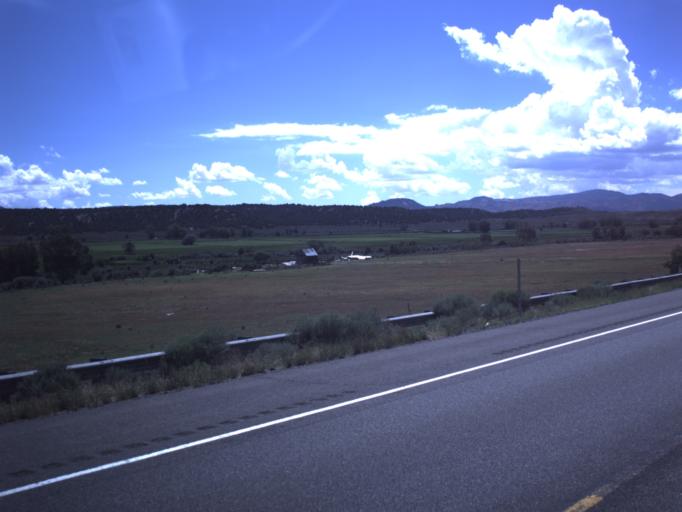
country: US
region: Utah
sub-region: Garfield County
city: Panguitch
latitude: 37.8143
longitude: -112.4034
